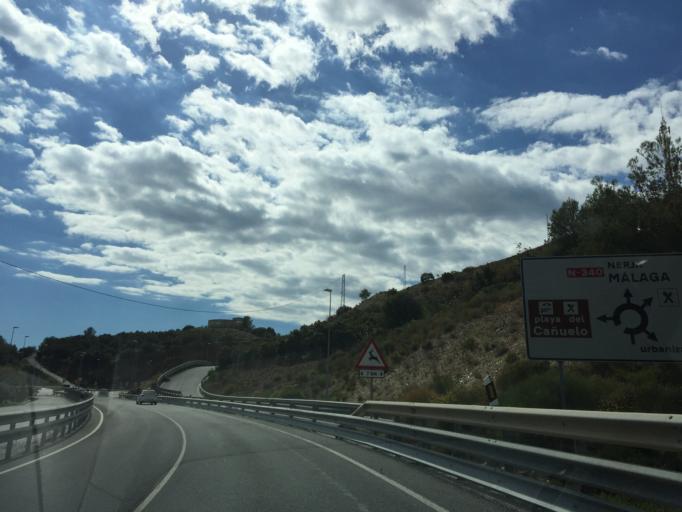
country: ES
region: Andalusia
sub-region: Provincia de Granada
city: La Herradura
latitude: 36.7521
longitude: -3.7820
